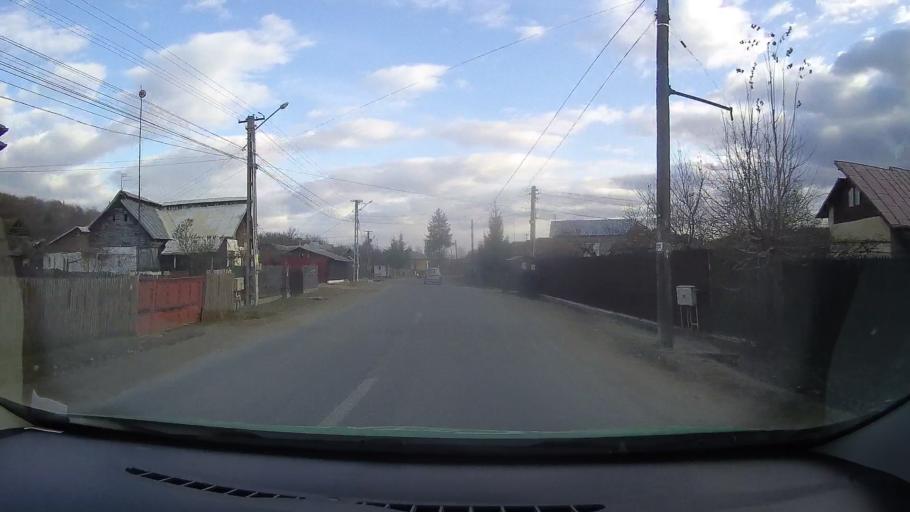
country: RO
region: Dambovita
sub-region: Comuna Gura Ocnitei
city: Gura Ocnitei
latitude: 44.9494
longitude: 25.5580
